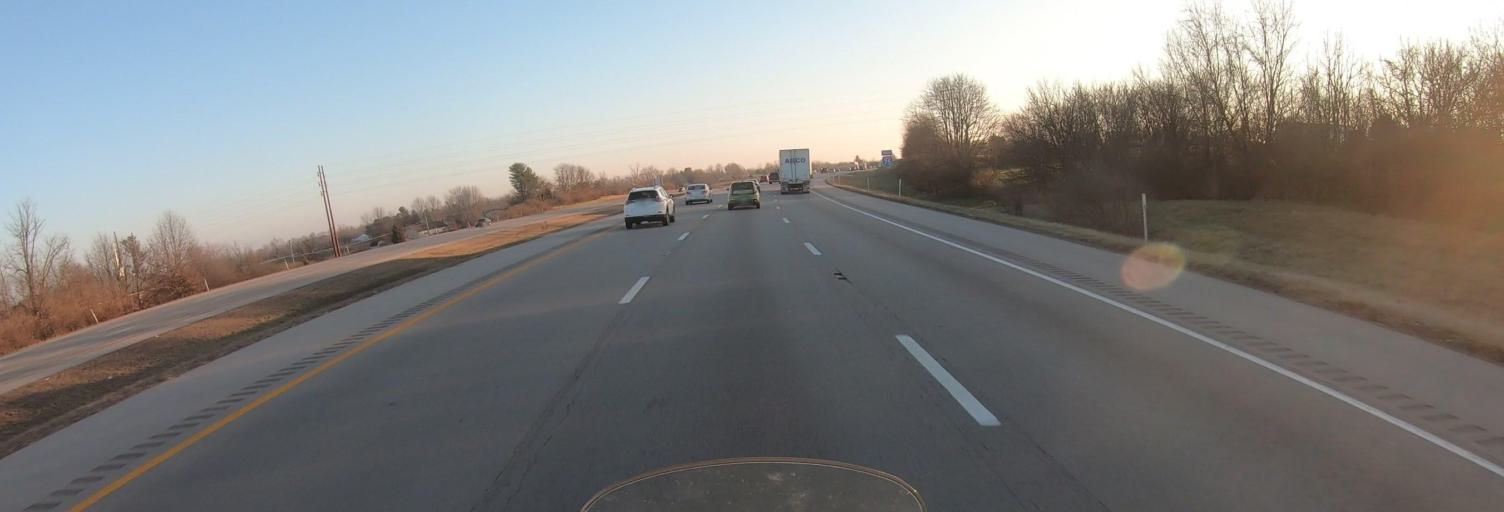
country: US
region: Kentucky
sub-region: Madison County
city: Richmond
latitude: 37.8369
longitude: -84.3239
